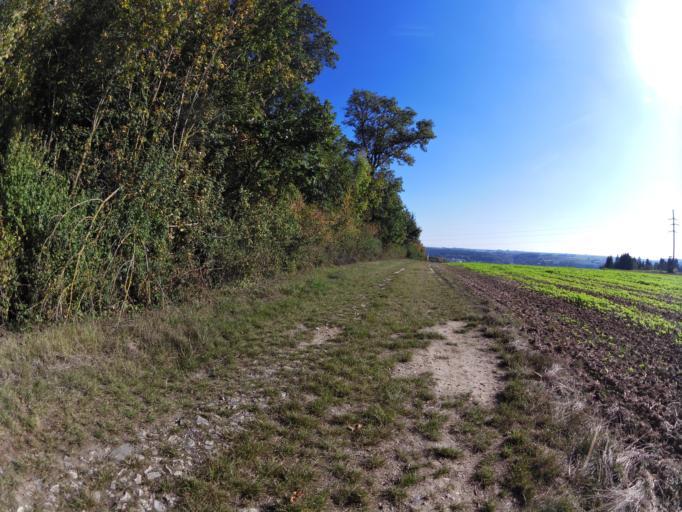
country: DE
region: Bavaria
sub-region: Regierungsbezirk Unterfranken
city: Ochsenfurt
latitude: 49.6782
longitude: 10.0638
